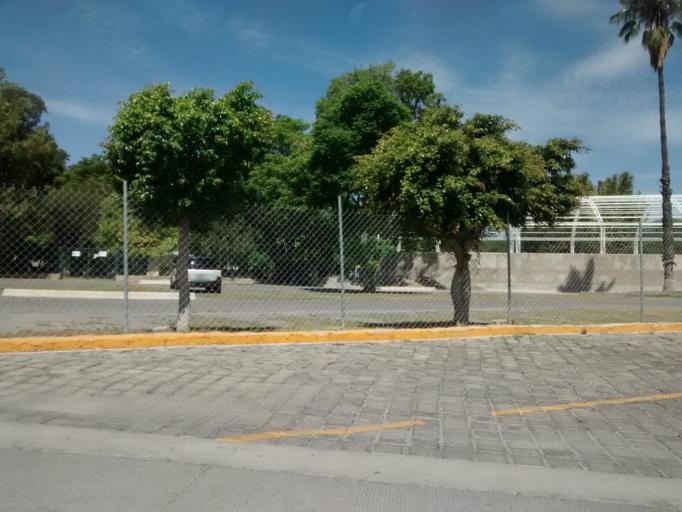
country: MX
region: Puebla
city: Tehuacan
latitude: 18.4703
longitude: -97.4147
